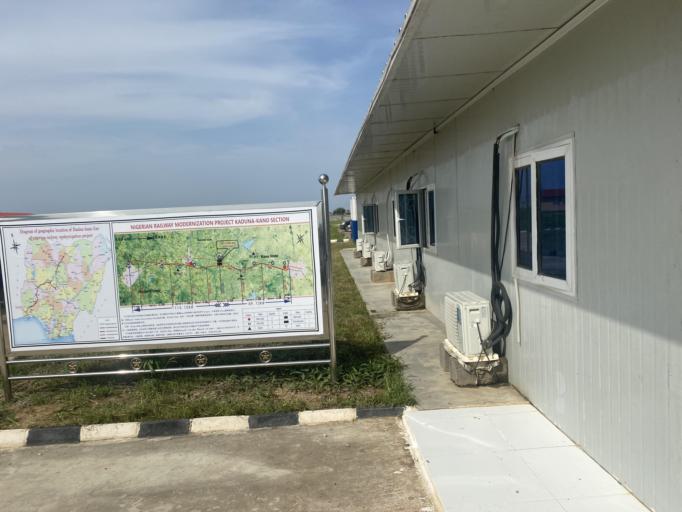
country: NG
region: Kano
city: Kumbotso
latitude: 11.9034
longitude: 8.4414
